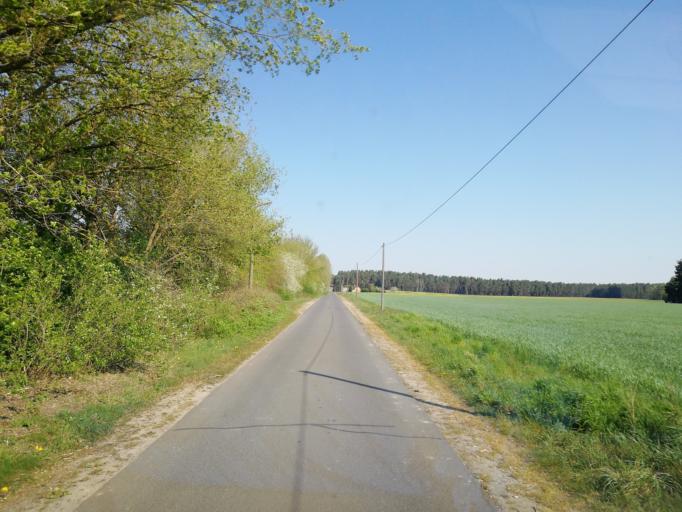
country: DE
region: Brandenburg
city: Sallgast
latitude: 51.6445
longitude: 13.8606
